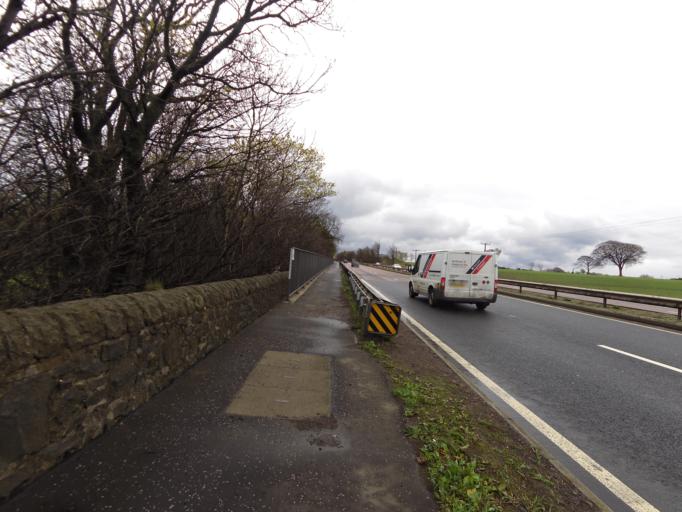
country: GB
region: Scotland
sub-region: Edinburgh
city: Queensferry
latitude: 55.9760
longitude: -3.3387
